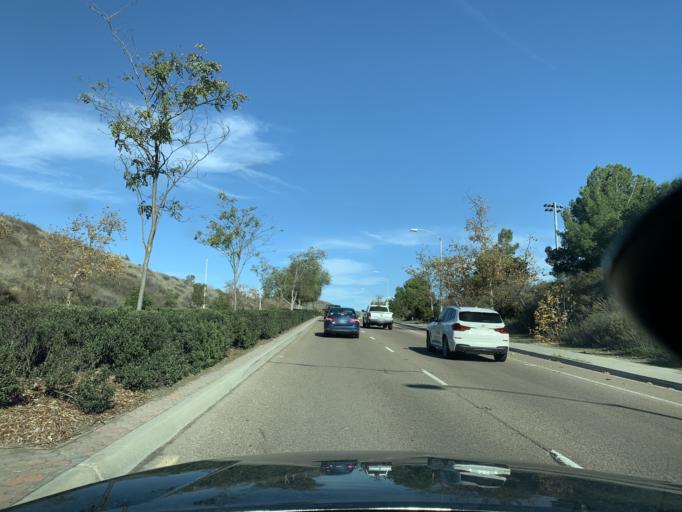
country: US
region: California
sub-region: San Diego County
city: Santee
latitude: 32.8463
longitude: -117.0232
